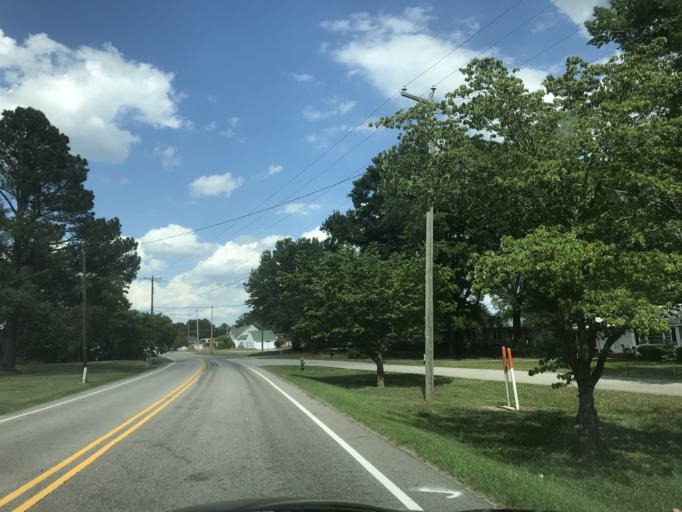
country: US
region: North Carolina
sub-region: Nash County
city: Spring Hope
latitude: 35.9595
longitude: -78.2562
